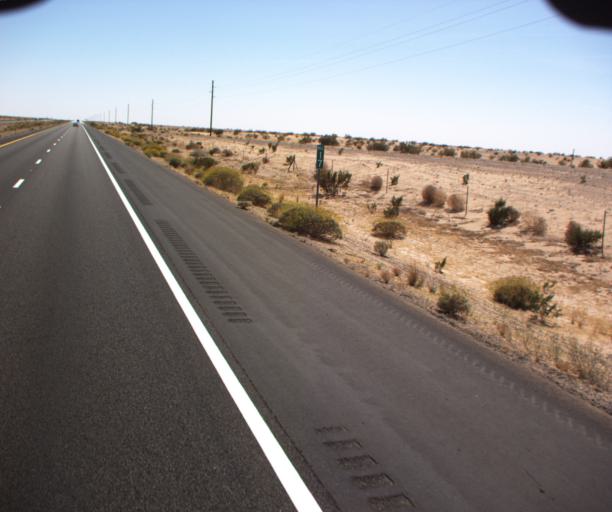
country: US
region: Arizona
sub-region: Yuma County
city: Somerton
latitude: 32.5361
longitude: -114.5623
